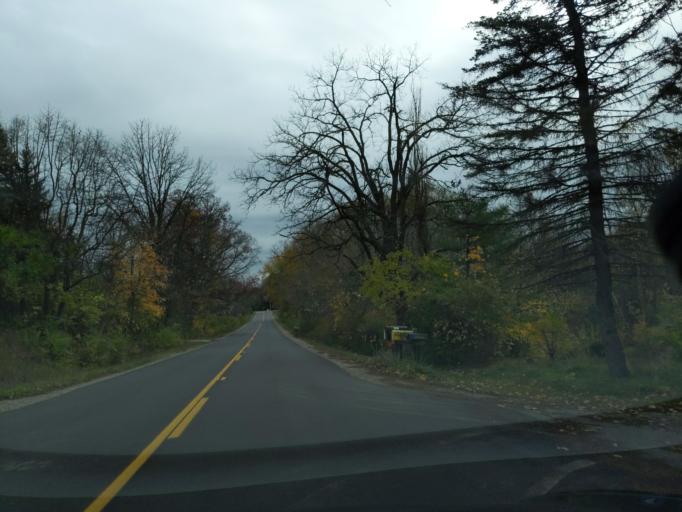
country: US
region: Michigan
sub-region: Eaton County
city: Eaton Rapids
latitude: 42.5269
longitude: -84.6211
